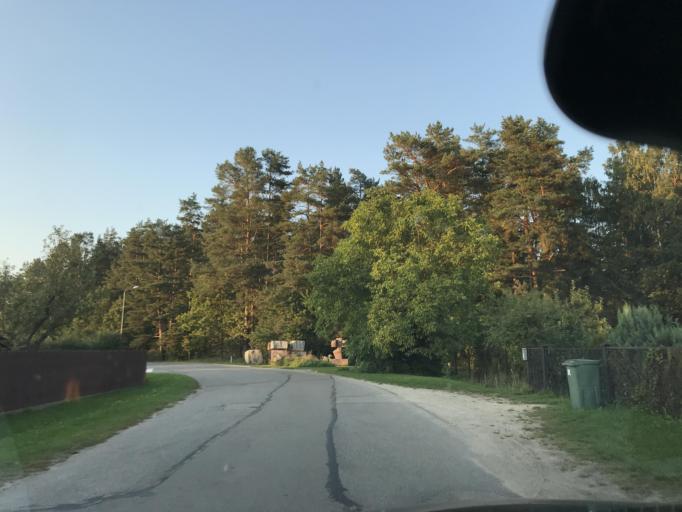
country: LV
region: Ikskile
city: Ikskile
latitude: 56.8283
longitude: 24.5052
